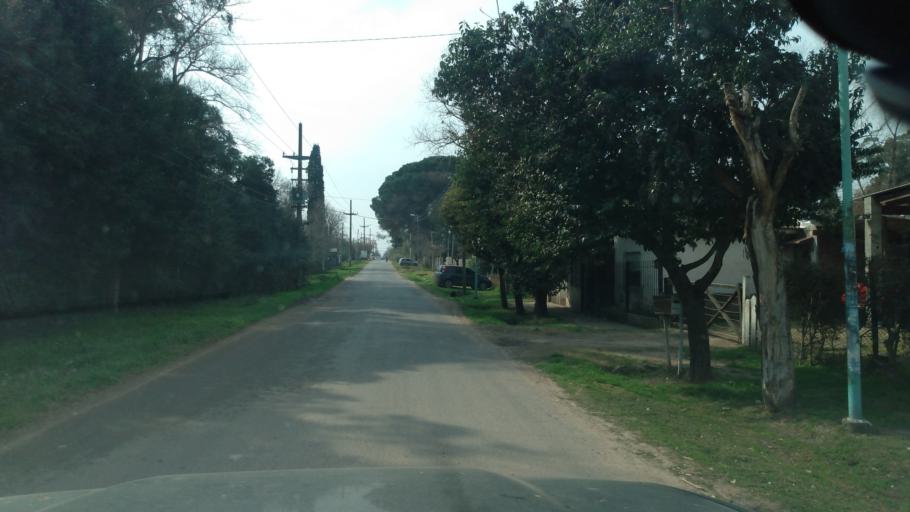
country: AR
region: Buenos Aires
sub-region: Partido de Lujan
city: Lujan
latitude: -34.4926
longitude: -59.0817
